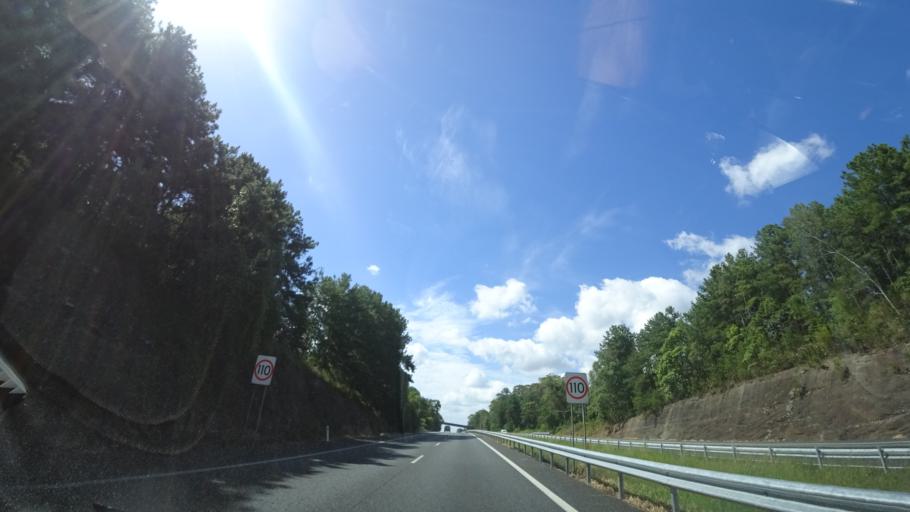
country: AU
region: Queensland
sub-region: Sunshine Coast
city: Woombye
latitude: -26.6597
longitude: 152.9947
